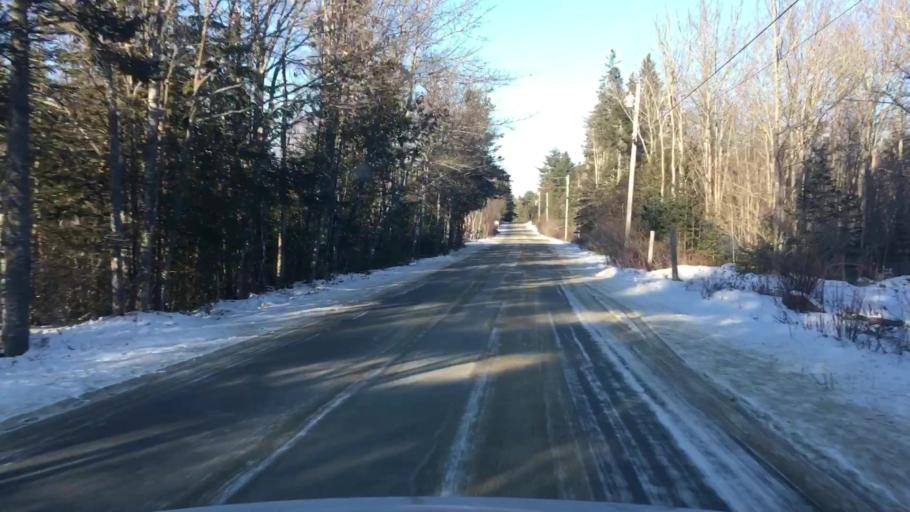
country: US
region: Maine
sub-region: Hancock County
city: Penobscot
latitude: 44.3907
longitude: -68.7153
